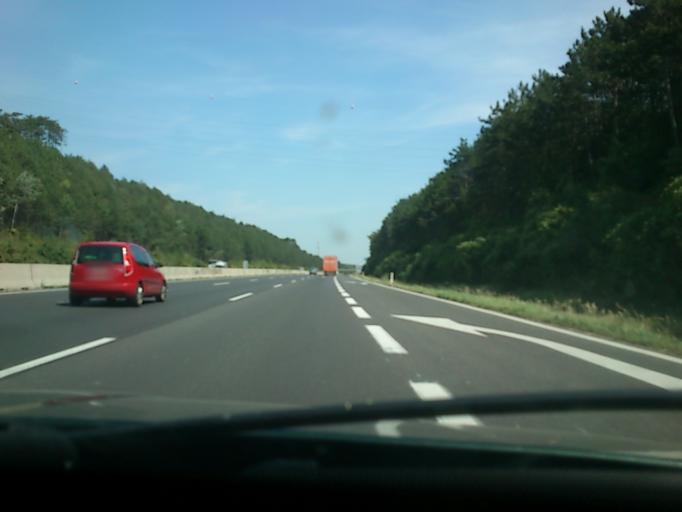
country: AT
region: Lower Austria
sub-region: Politischer Bezirk Wiener Neustadt
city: Theresienfeld
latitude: 47.8492
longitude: 16.1820
